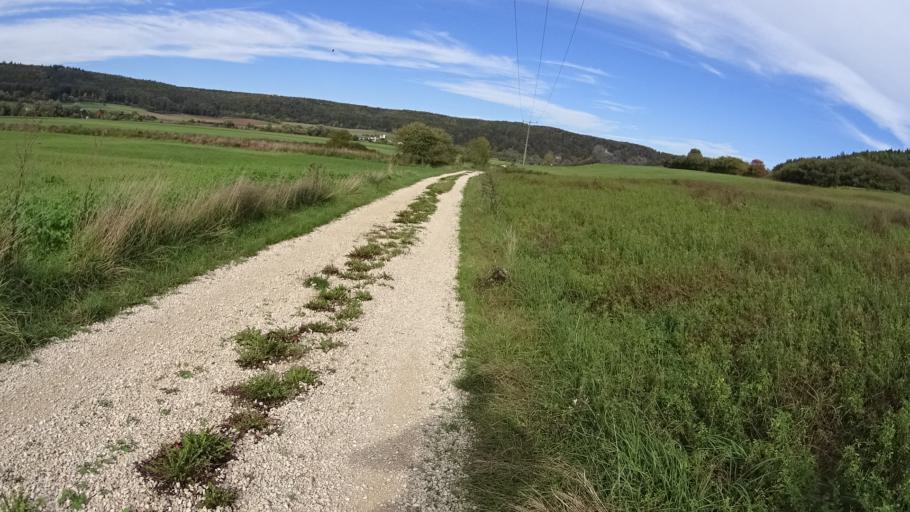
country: DE
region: Bavaria
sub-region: Upper Bavaria
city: Walting
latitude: 48.9284
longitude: 11.3118
